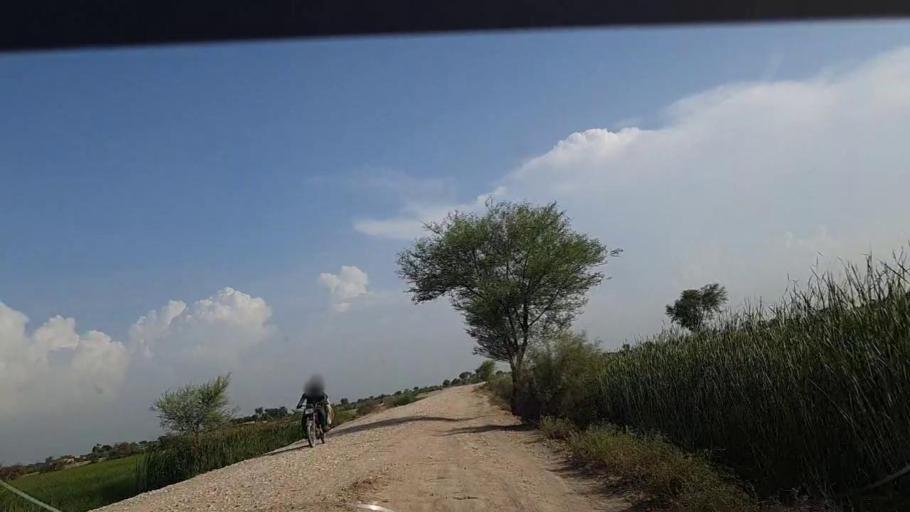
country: PK
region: Sindh
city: Khanpur
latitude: 27.8520
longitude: 69.3774
